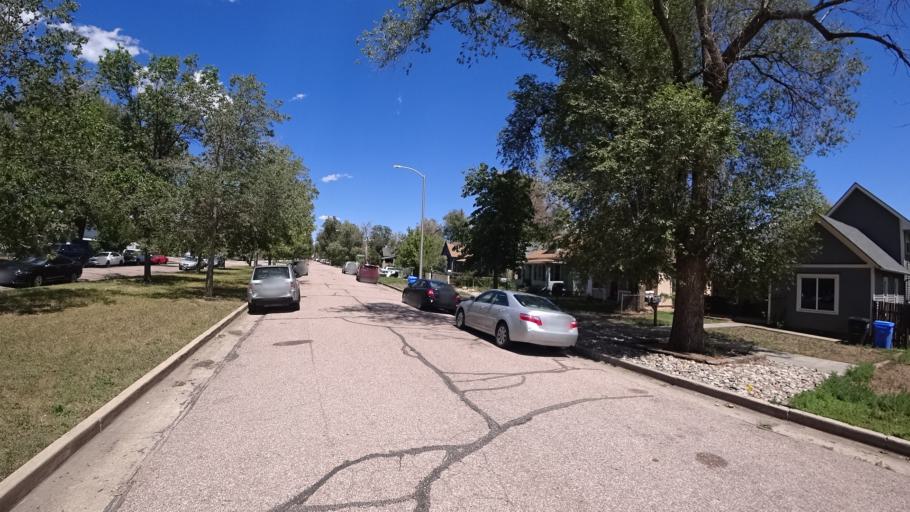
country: US
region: Colorado
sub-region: El Paso County
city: Colorado Springs
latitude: 38.8210
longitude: -104.8260
